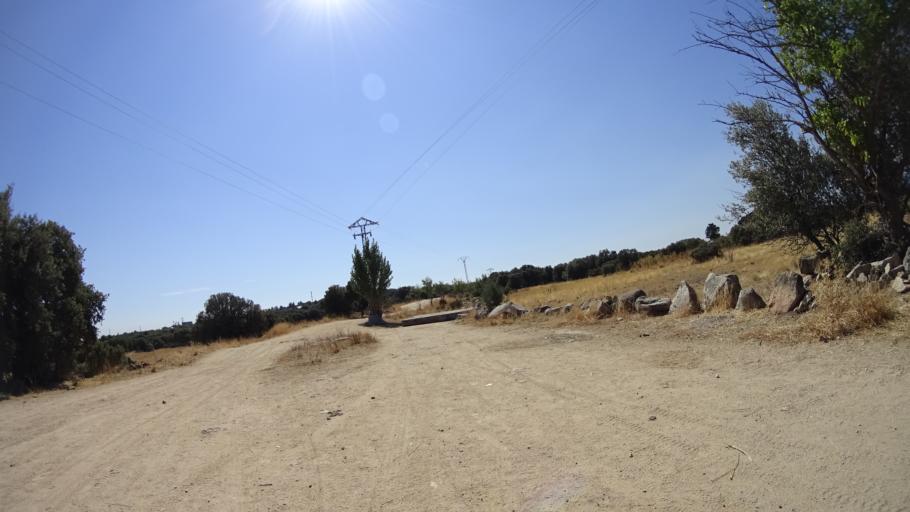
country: ES
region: Madrid
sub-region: Provincia de Madrid
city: Collado-Villalba
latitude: 40.6124
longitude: -4.0108
